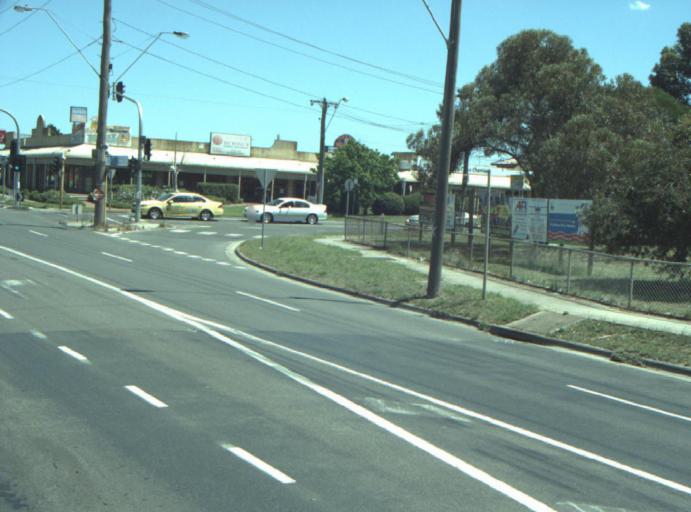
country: AU
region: Victoria
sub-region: Greater Geelong
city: Bell Park
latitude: -38.1103
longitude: 144.3436
